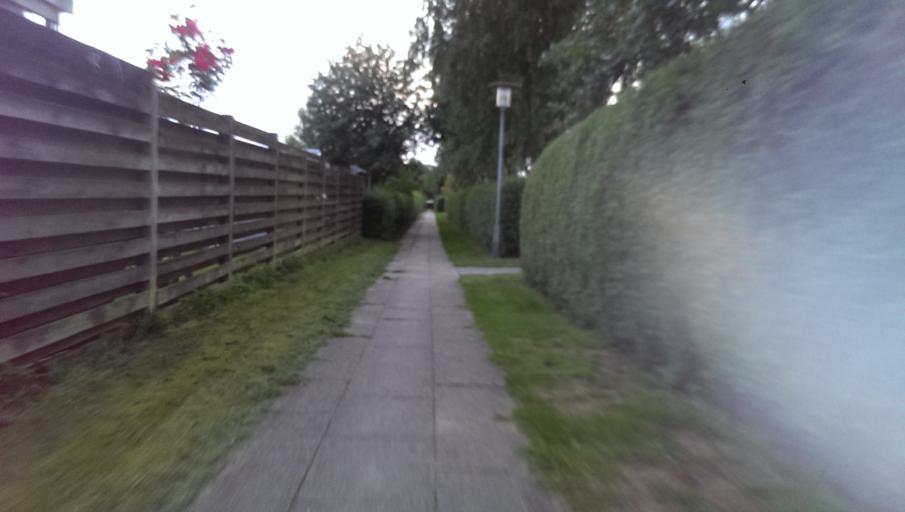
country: DK
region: South Denmark
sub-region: Esbjerg Kommune
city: Tjaereborg
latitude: 55.4723
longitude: 8.5719
